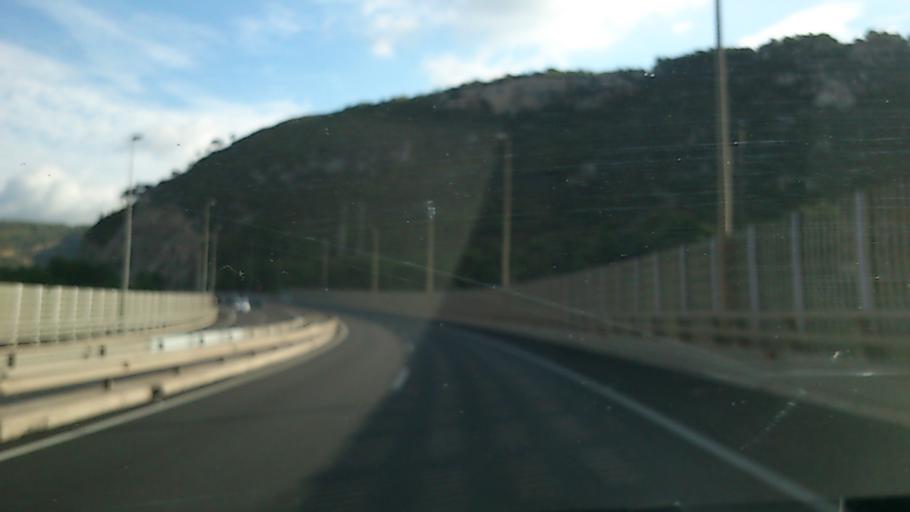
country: ES
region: Catalonia
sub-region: Provincia de Barcelona
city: Sitges
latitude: 41.2440
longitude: 1.8593
